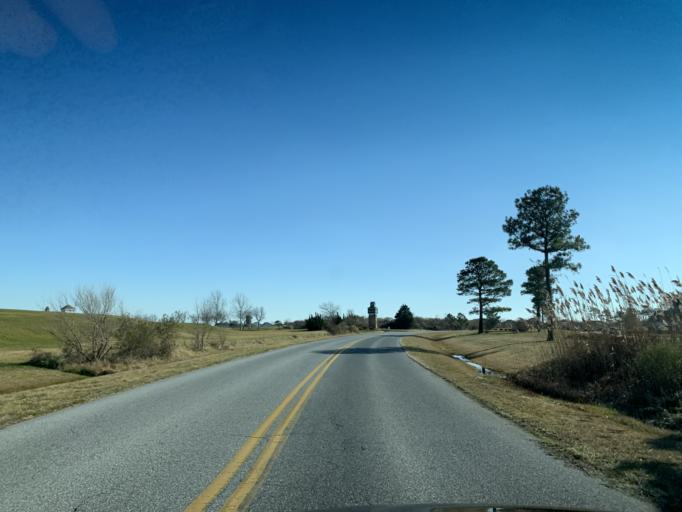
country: US
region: Maryland
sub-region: Worcester County
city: Ocean Pines
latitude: 38.4103
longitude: -75.1102
